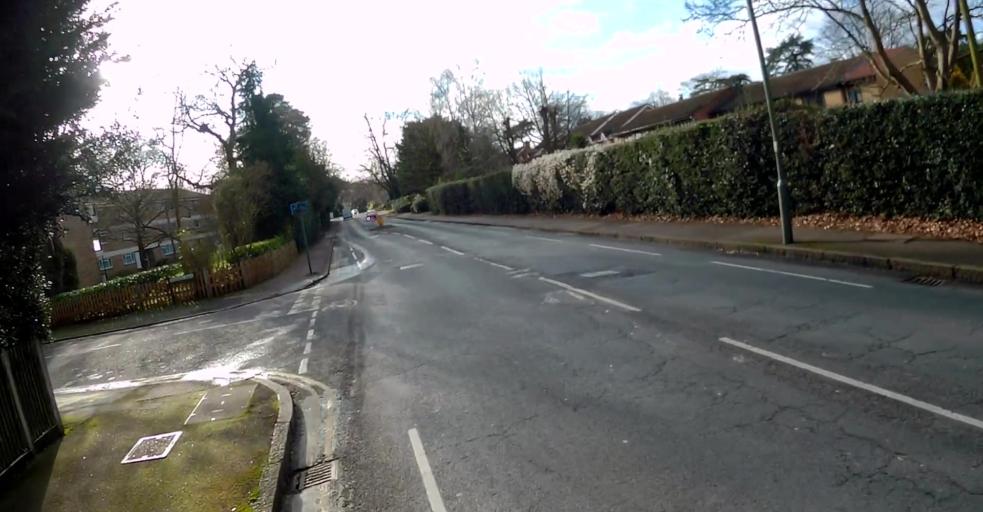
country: GB
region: England
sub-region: Surrey
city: Weybridge
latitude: 51.3764
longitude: -0.4361
